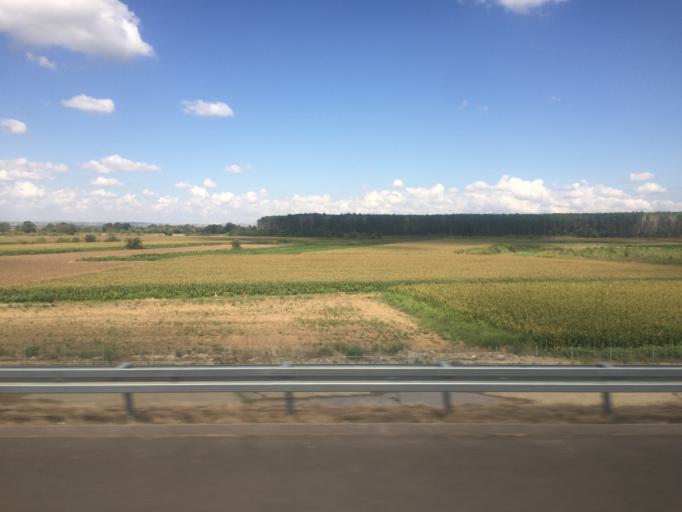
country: TR
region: Bursa
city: Karacabey
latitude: 40.1403
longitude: 28.3015
